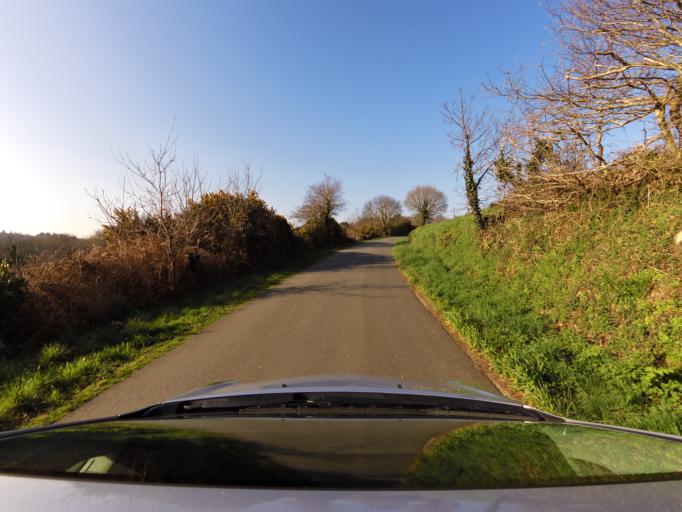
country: FR
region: Brittany
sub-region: Departement du Morbihan
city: Guidel-Plage
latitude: 47.7759
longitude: -3.5004
